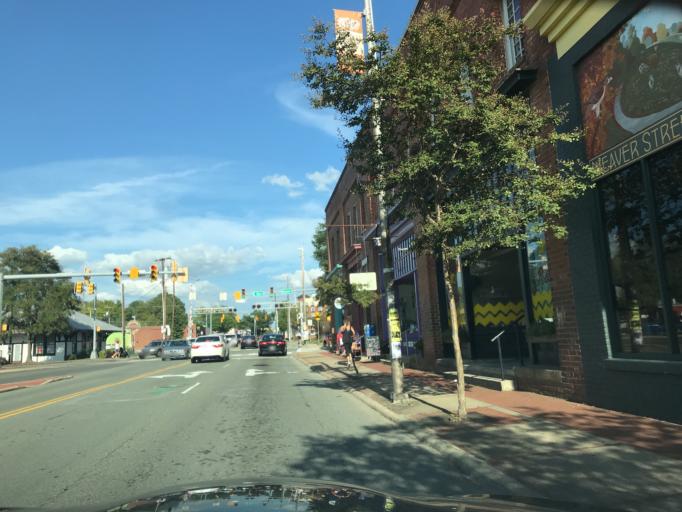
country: US
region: North Carolina
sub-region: Orange County
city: Carrboro
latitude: 35.9105
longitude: -79.0707
